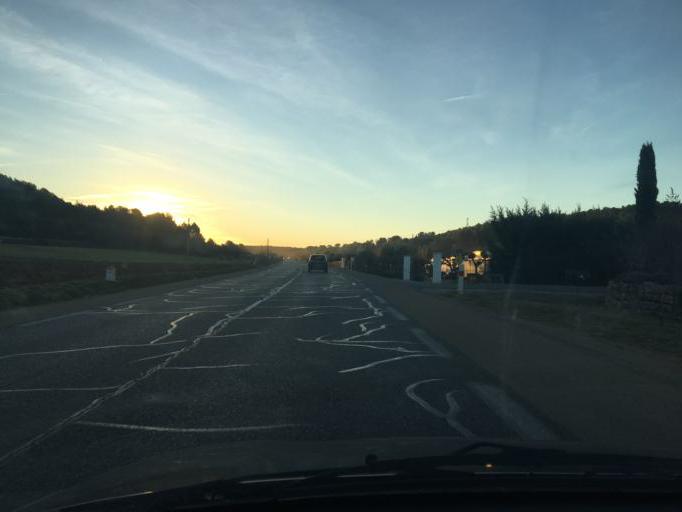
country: FR
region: Provence-Alpes-Cote d'Azur
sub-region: Departement du Var
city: Lorgues
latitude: 43.4753
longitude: 6.3755
